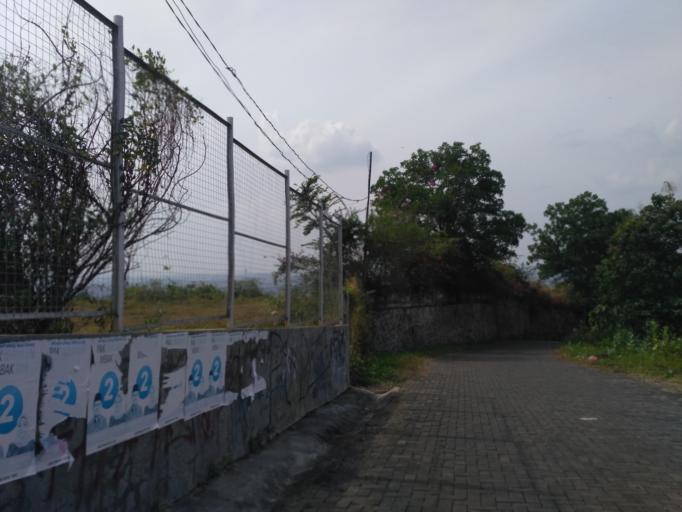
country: ID
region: Central Java
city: Semarang
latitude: -7.0273
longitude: 110.4422
